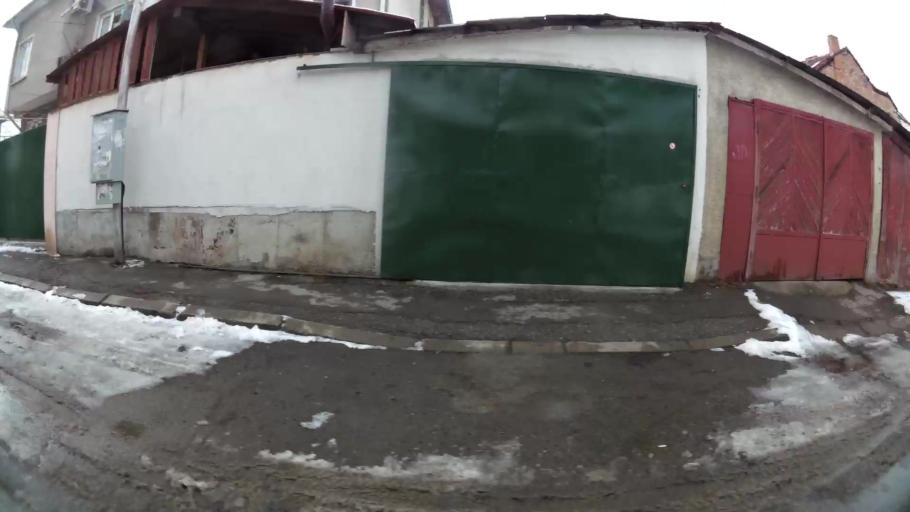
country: BG
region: Sofia-Capital
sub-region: Stolichna Obshtina
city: Sofia
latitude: 42.7057
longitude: 23.3786
